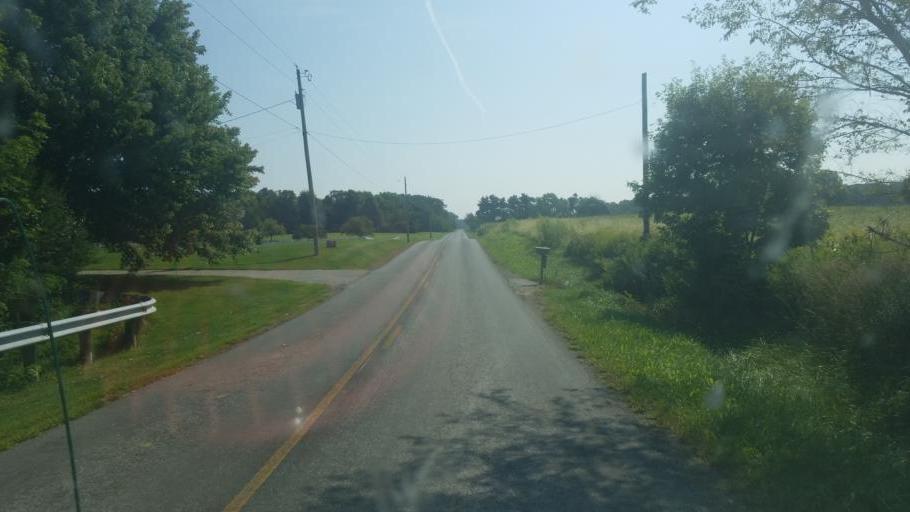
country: US
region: Ohio
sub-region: Wayne County
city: West Salem
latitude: 41.0062
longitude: -82.1131
